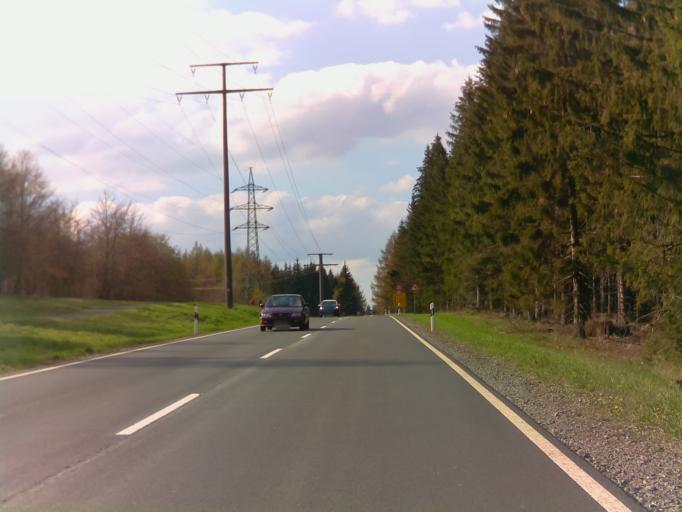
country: DE
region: Bavaria
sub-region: Upper Franconia
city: Tettau
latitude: 50.4763
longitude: 11.3062
